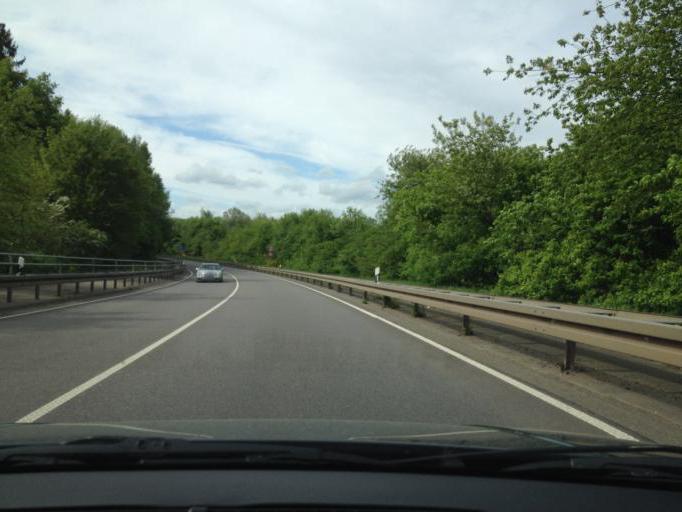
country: DE
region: Saarland
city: Bexbach
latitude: 49.3401
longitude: 7.2276
